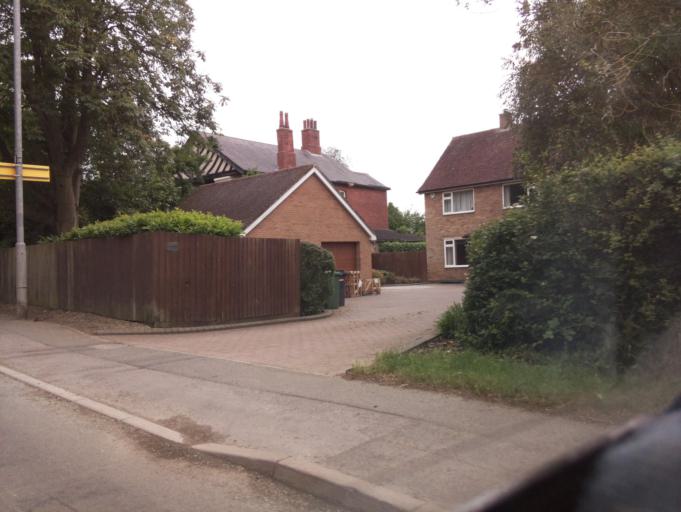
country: GB
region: England
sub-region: Leicestershire
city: Melton Mowbray
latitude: 52.7547
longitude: -0.8796
